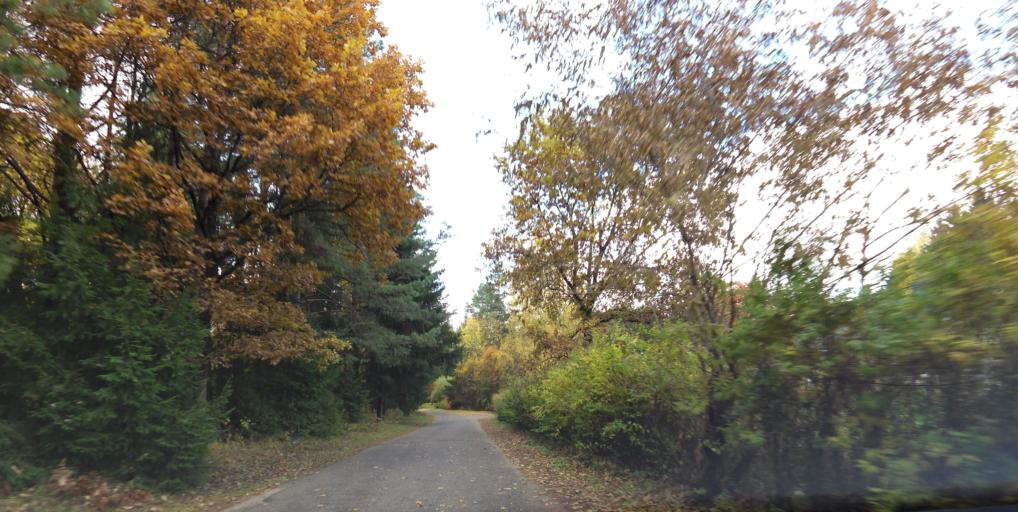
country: LT
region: Vilnius County
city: Vilkpede
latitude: 54.6480
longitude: 25.2547
